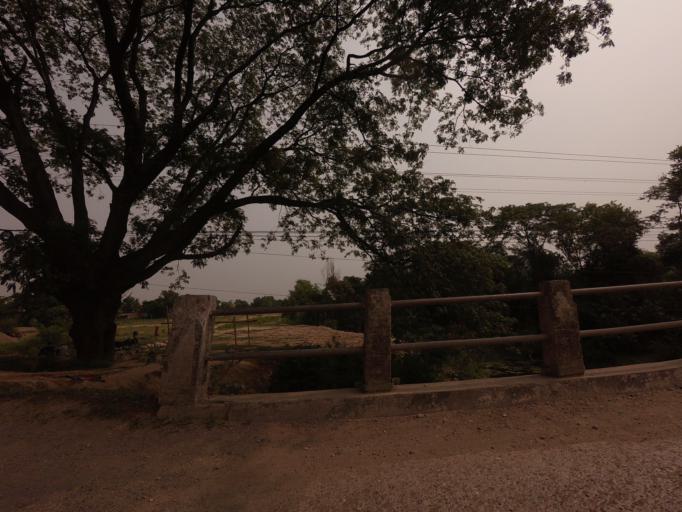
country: NP
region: Western Region
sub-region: Lumbini Zone
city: Bhairahawa
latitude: 27.5112
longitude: 83.4068
